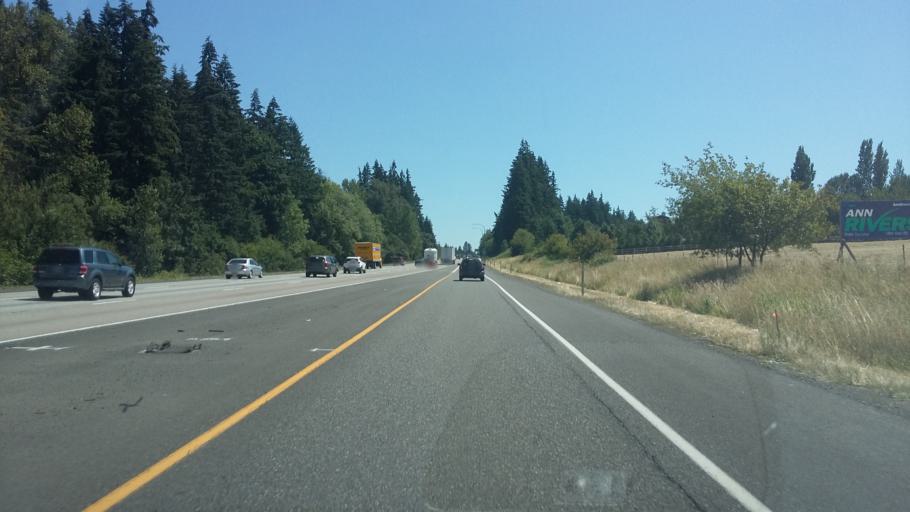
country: US
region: Washington
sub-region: Clark County
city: Mount Vista
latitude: 45.7793
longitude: -122.6732
